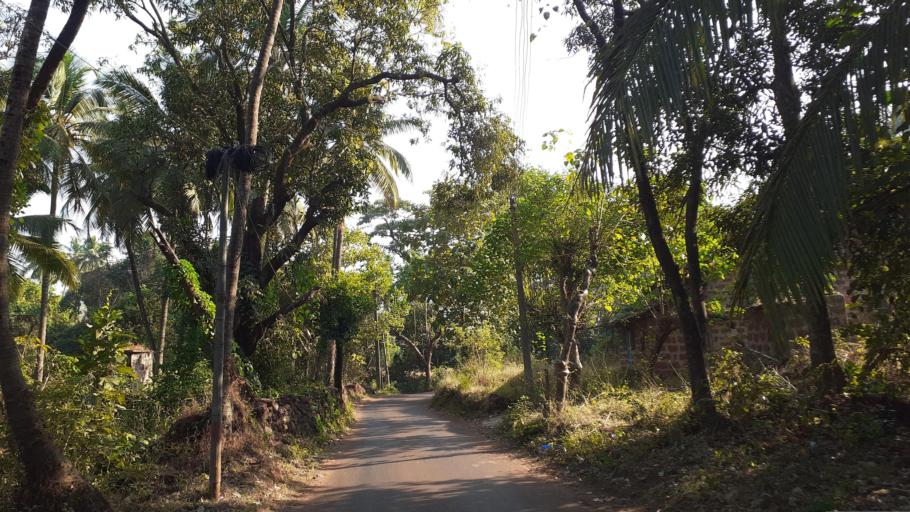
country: IN
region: Maharashtra
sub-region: Ratnagiri
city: Ratnagiri
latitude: 17.2144
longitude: 73.2482
